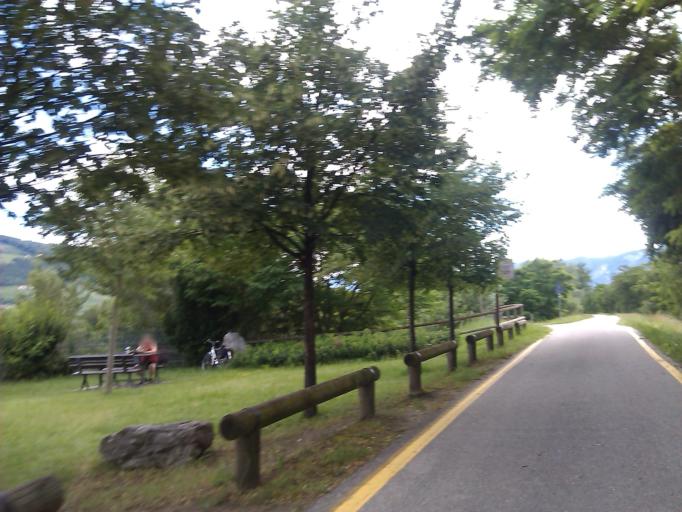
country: IT
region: Trentino-Alto Adige
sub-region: Provincia di Trento
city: San Michele All'Adige
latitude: 46.1887
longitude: 11.1180
